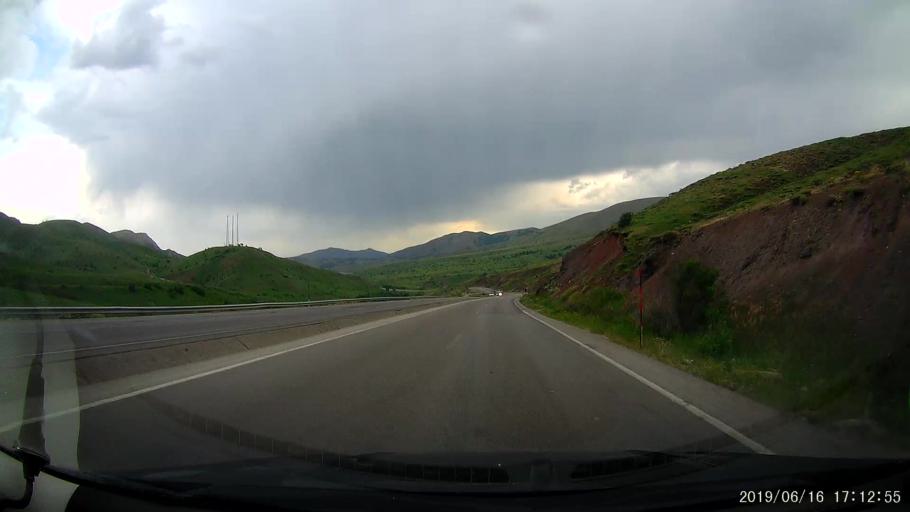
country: TR
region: Erzurum
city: Askale
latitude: 39.8593
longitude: 40.6097
